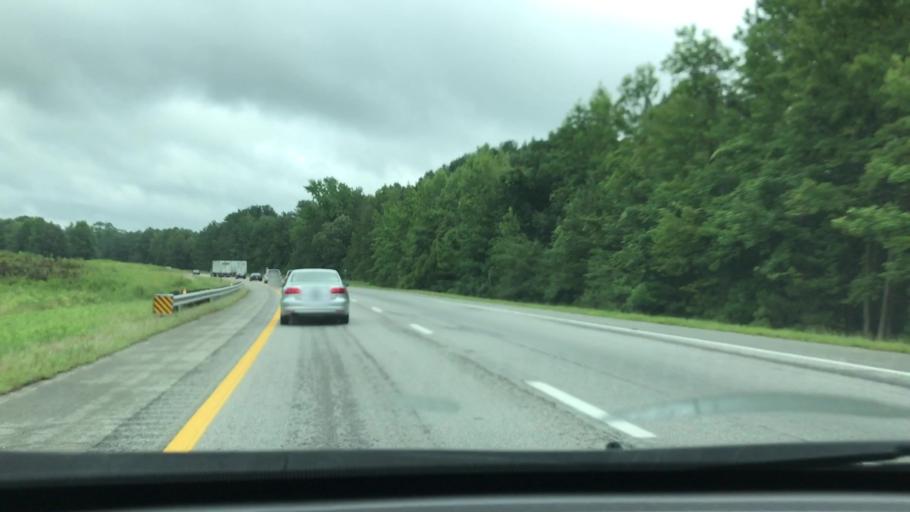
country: US
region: Virginia
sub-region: City of Emporia
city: Emporia
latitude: 36.7687
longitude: -77.4668
